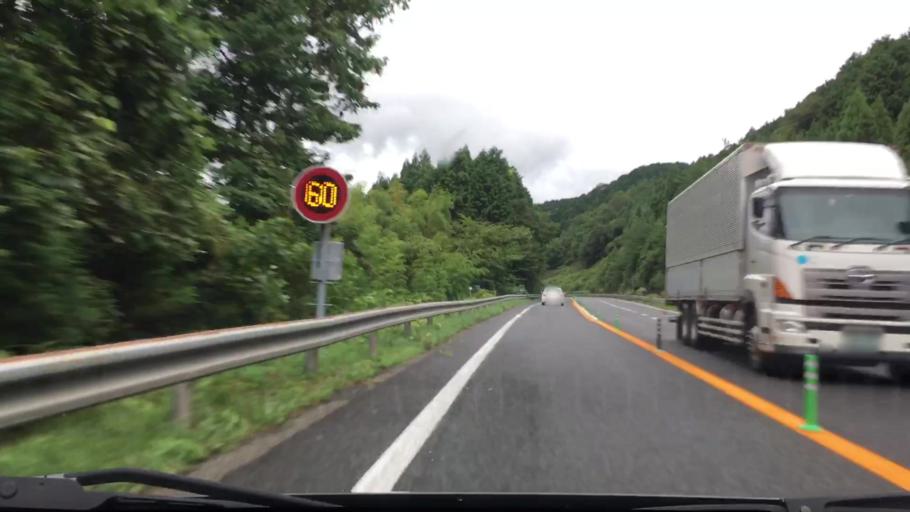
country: JP
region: Hyogo
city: Nishiwaki
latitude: 35.0973
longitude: 134.7765
